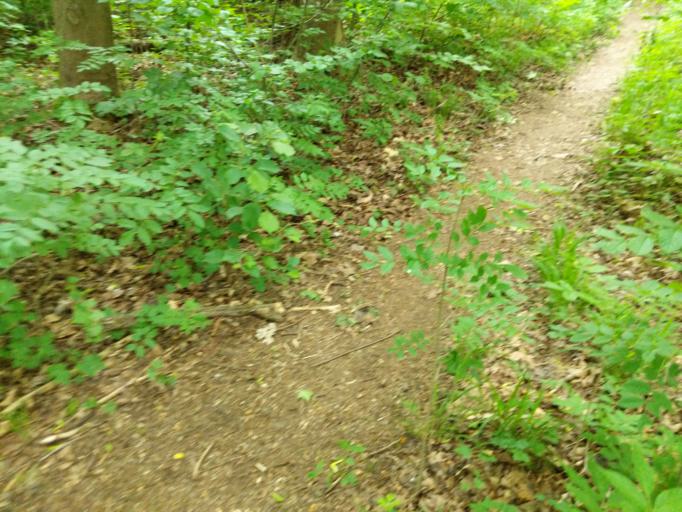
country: DE
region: Bavaria
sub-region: Upper Bavaria
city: Neuried
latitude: 48.1030
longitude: 11.5077
